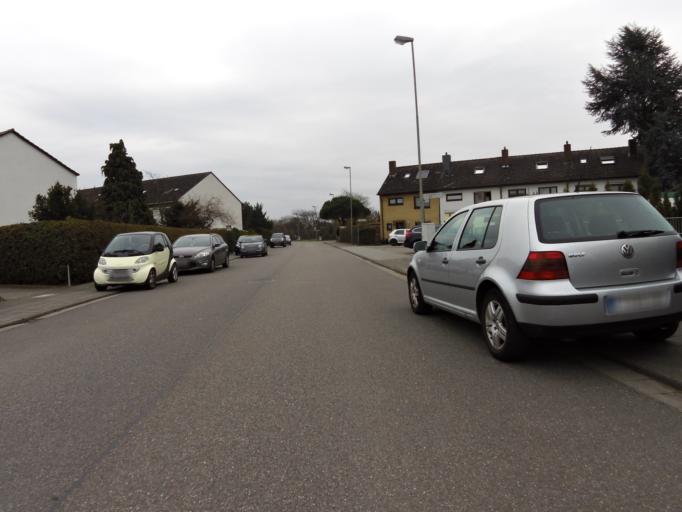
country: DE
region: Rheinland-Pfalz
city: Frankenthal
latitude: 49.5441
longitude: 8.3695
